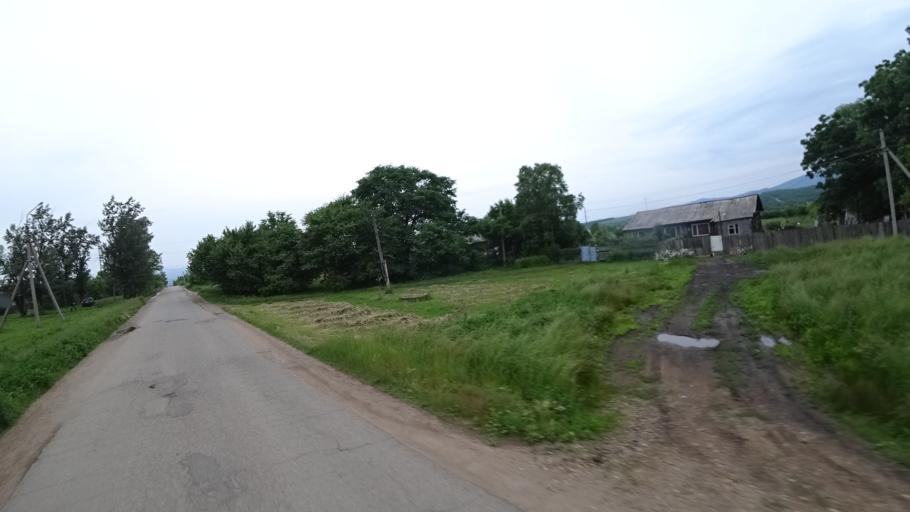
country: RU
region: Primorskiy
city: Novosysoyevka
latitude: 44.2306
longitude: 133.3607
